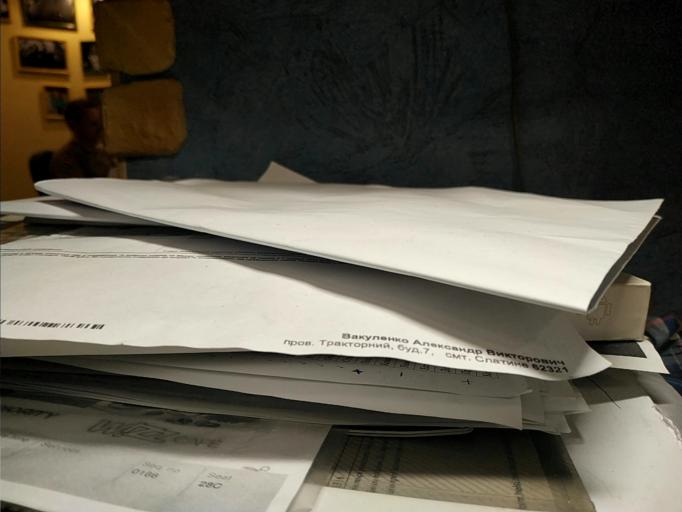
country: RU
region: Tverskaya
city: Zubtsov
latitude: 56.1199
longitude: 34.5750
